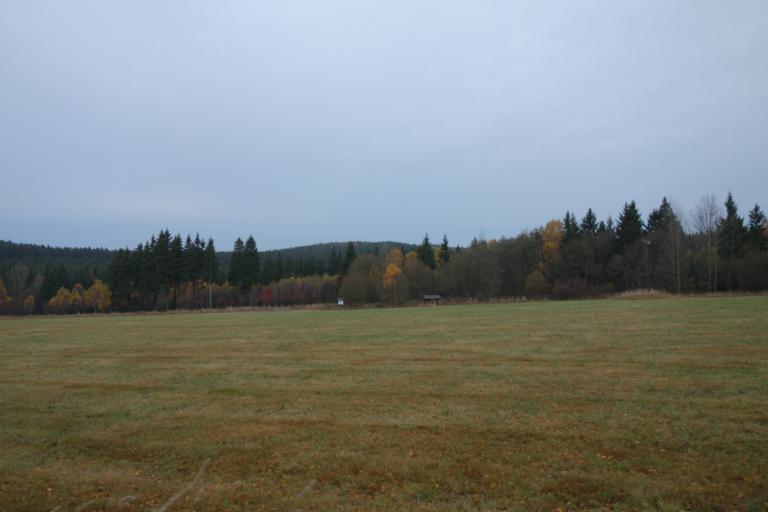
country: DE
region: Saxony
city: Johstadt
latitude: 50.5008
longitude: 13.0651
